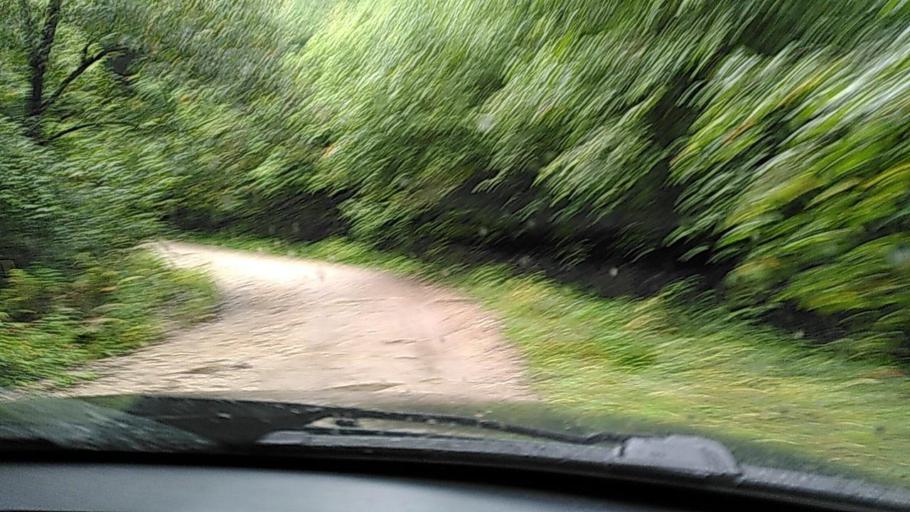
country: RU
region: Kabardino-Balkariya
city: Belaya Rechka
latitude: 43.4020
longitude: 43.4629
